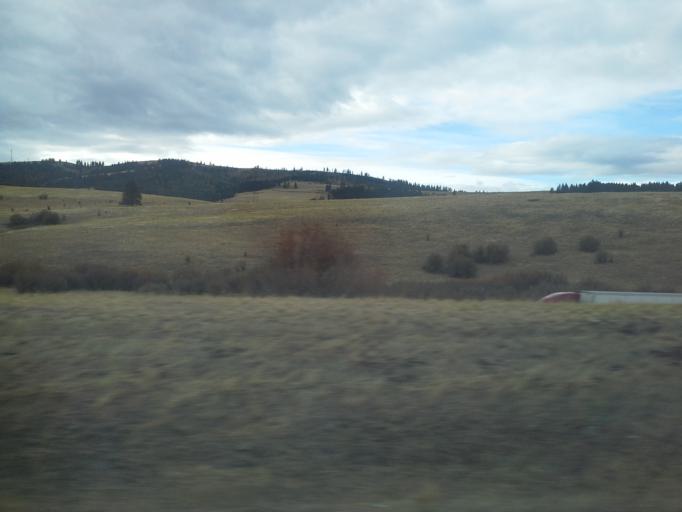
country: US
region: Oregon
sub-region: Union County
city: Union
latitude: 45.1918
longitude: -118.0021
